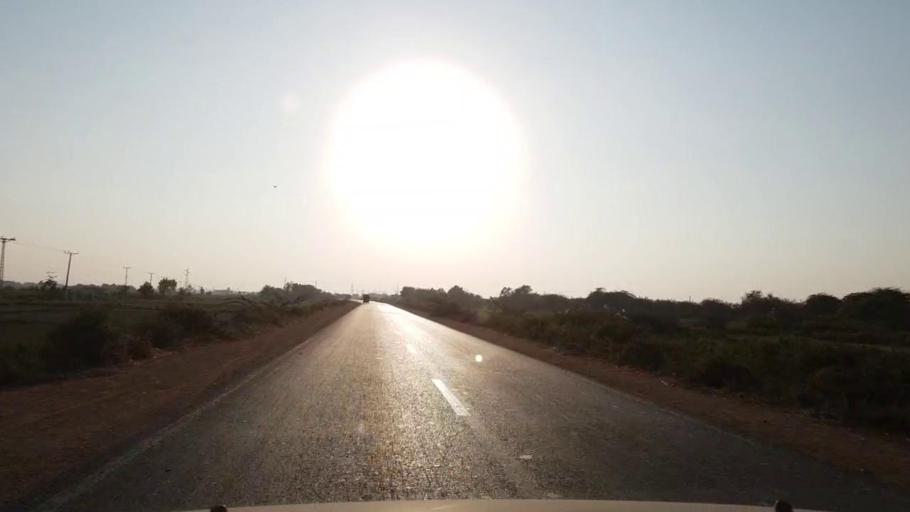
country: PK
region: Sindh
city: Daro Mehar
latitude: 24.6343
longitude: 68.1083
